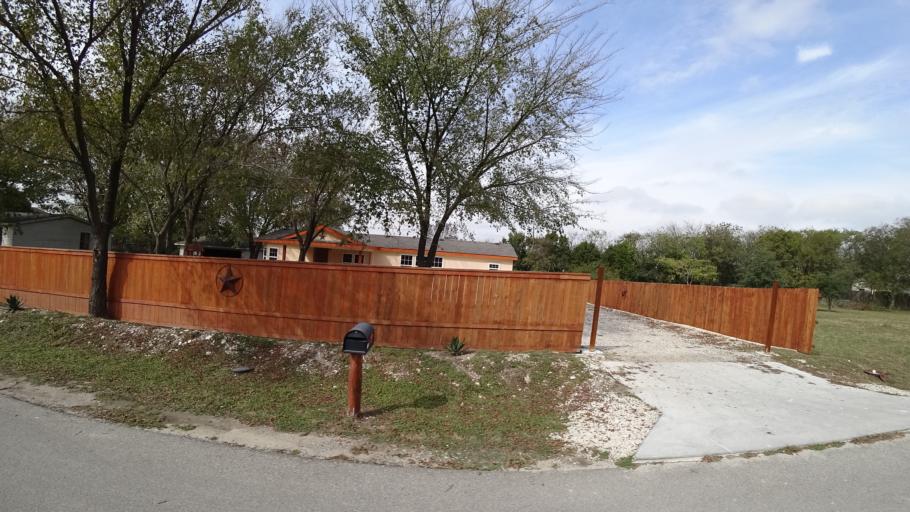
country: US
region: Texas
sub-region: Travis County
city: Wells Branch
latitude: 30.4499
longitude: -97.6708
